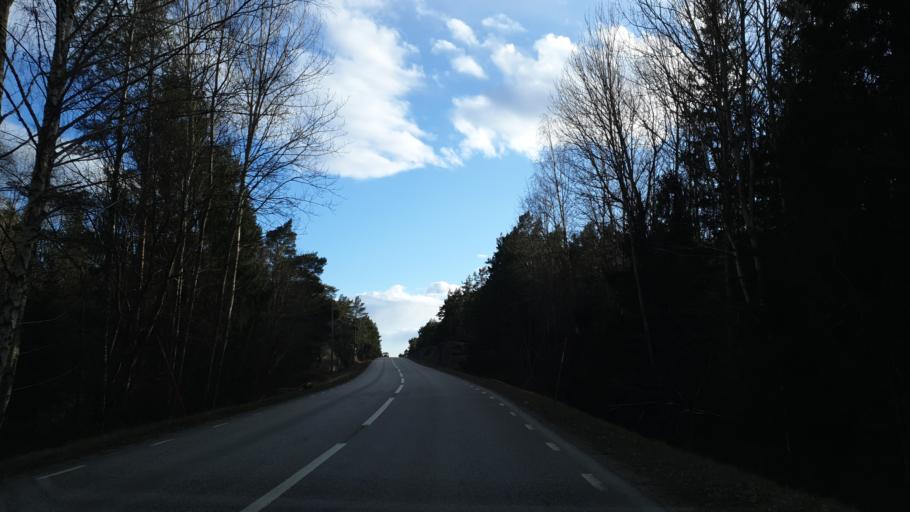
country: SE
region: Stockholm
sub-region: Varmdo Kommun
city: Holo
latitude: 59.3018
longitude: 18.6746
